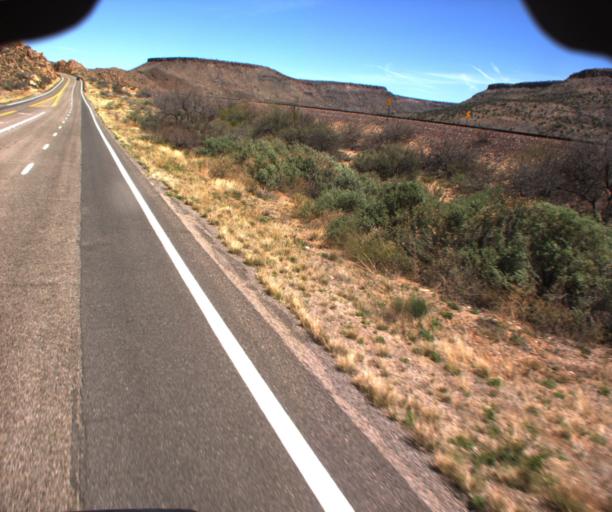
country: US
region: Arizona
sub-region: Mohave County
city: Peach Springs
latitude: 35.4077
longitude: -113.6493
